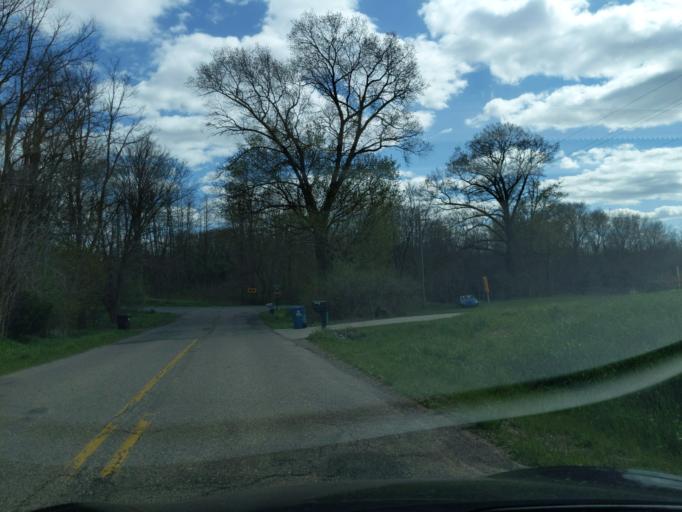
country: US
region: Michigan
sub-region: Ingham County
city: Leslie
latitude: 42.3941
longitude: -84.5269
